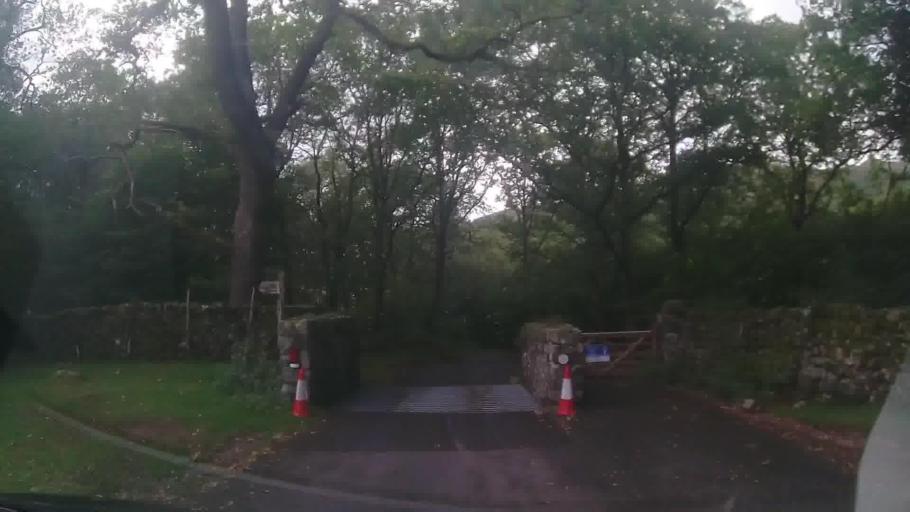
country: GB
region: England
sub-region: Cumbria
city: Millom
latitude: 54.3994
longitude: -3.2131
